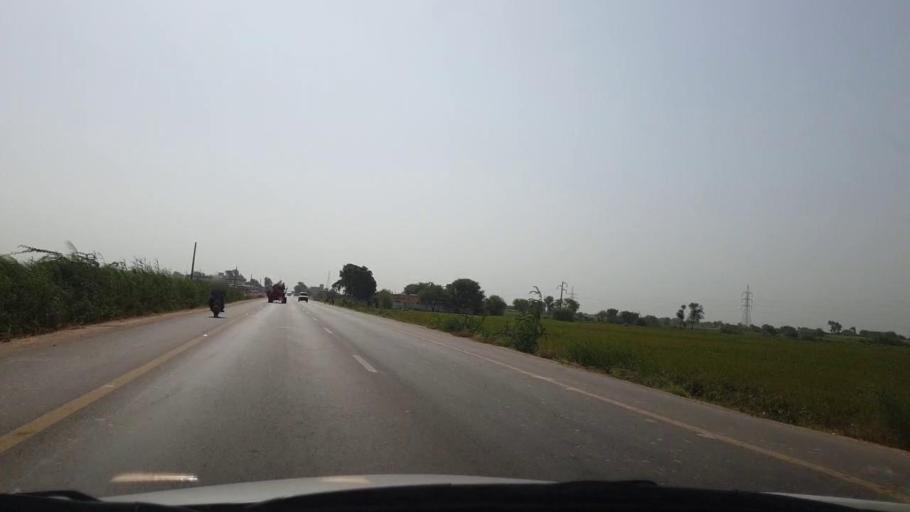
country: PK
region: Sindh
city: Tando Muhammad Khan
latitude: 25.1064
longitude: 68.5847
